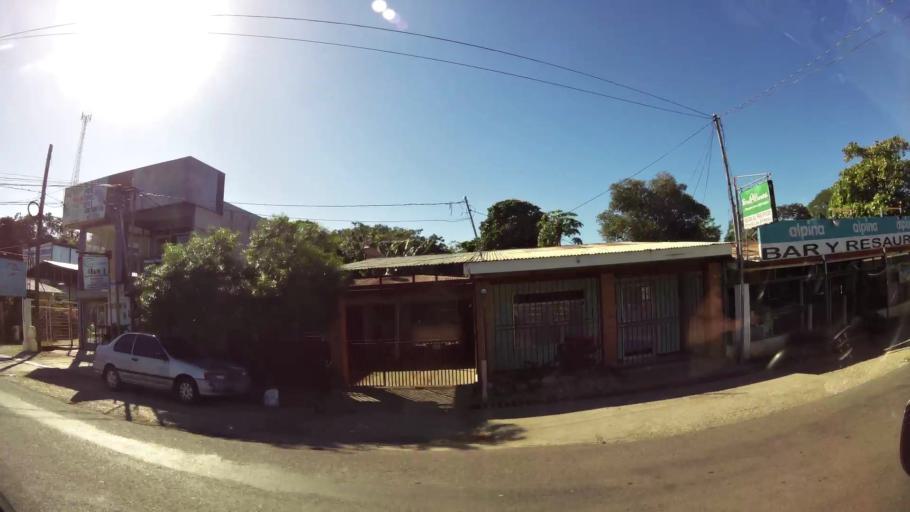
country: CR
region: Guanacaste
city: Belen
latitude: 10.3684
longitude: -85.7735
